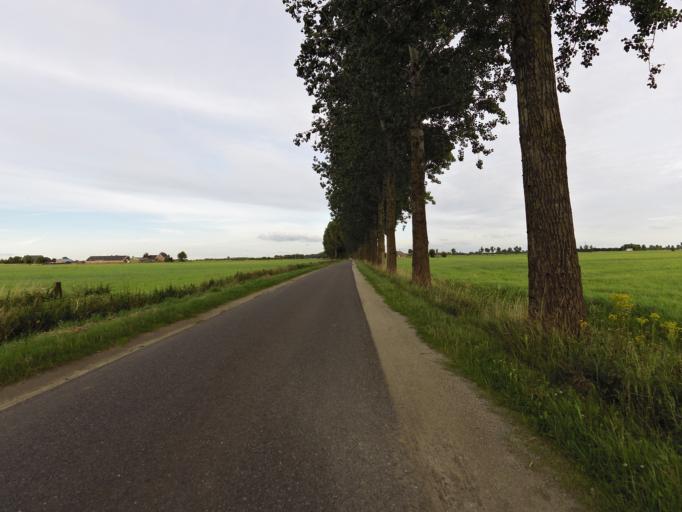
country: NL
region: Gelderland
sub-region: Gemeente Zevenaar
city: Zevenaar
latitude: 51.9736
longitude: 6.0830
